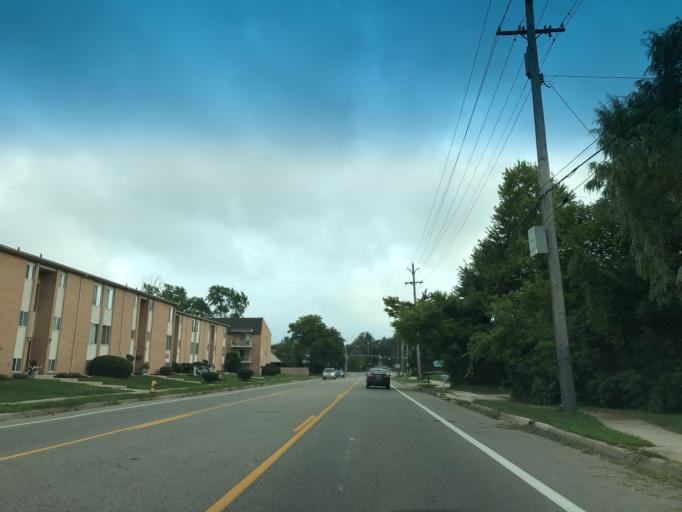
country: US
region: Michigan
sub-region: Washtenaw County
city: Ypsilanti
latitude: 42.2472
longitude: -83.6609
